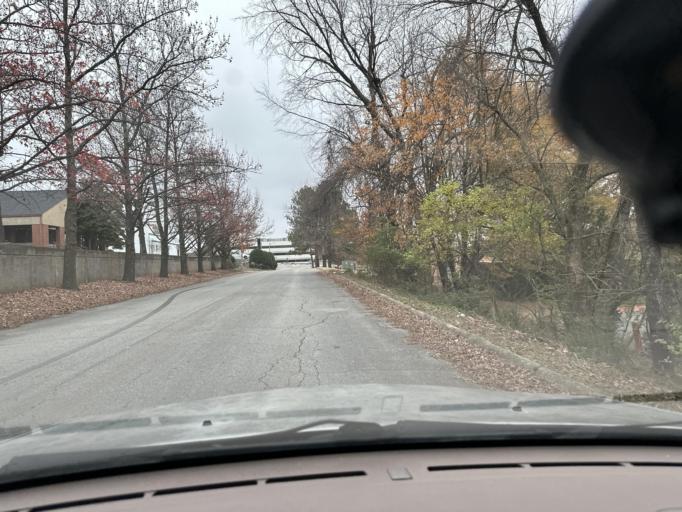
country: US
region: Arkansas
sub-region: Washington County
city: Johnson
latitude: 36.1248
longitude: -94.1469
